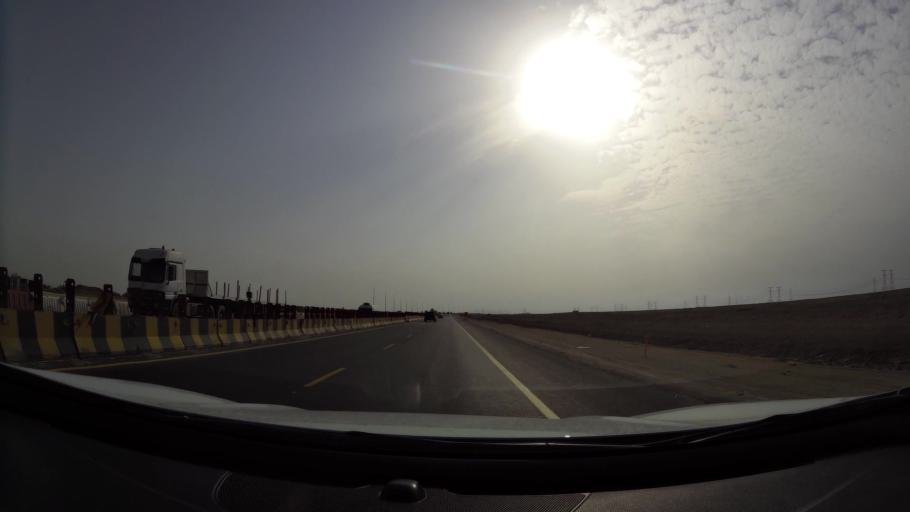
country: AE
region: Abu Dhabi
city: Abu Dhabi
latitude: 24.2398
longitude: 54.4647
